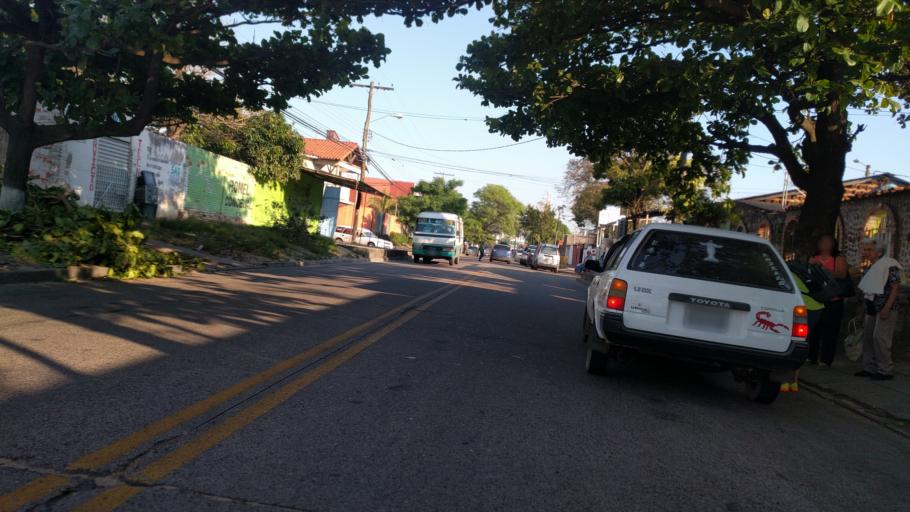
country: BO
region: Santa Cruz
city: Santa Cruz de la Sierra
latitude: -17.8092
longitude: -63.1688
